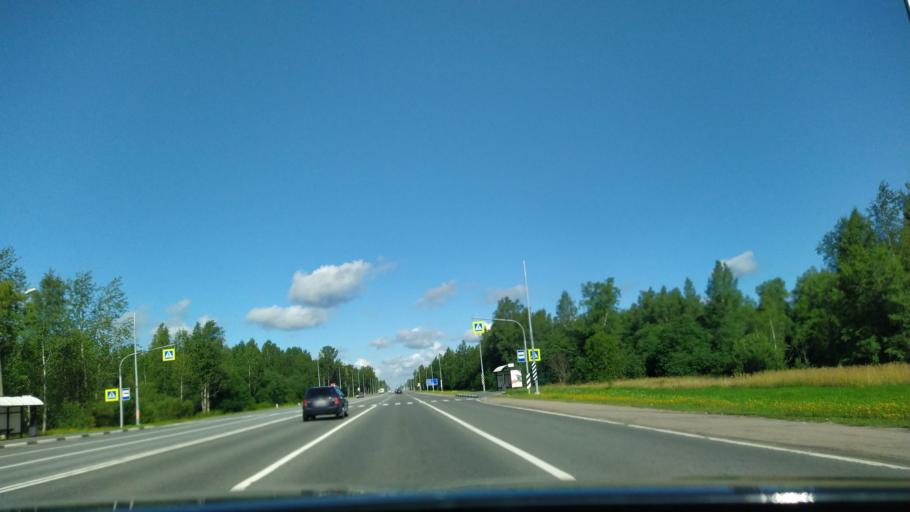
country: RU
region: Leningrad
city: Tosno
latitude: 59.5716
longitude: 30.8214
